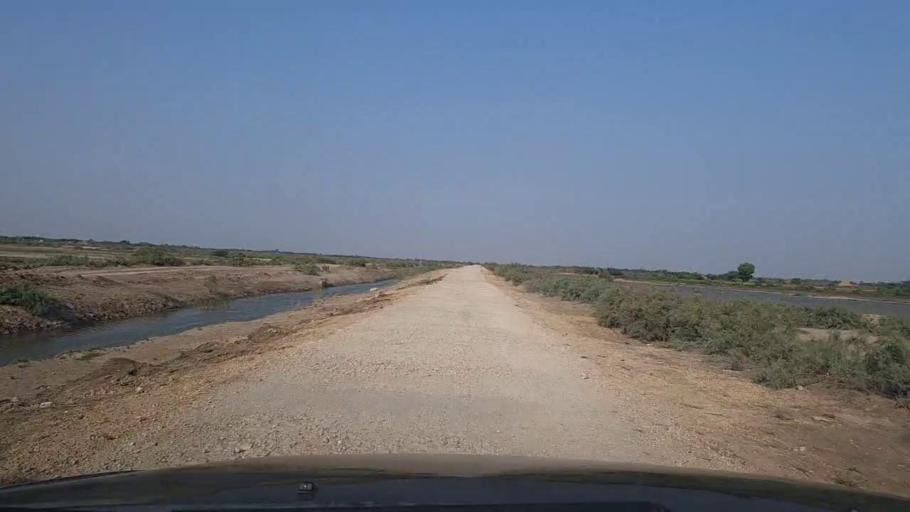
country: PK
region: Sindh
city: Mirpur Sakro
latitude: 24.6442
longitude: 67.7527
